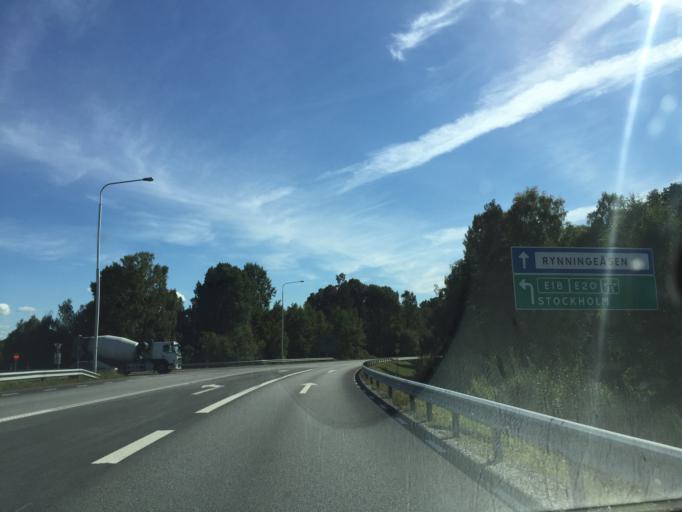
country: SE
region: OErebro
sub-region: Orebro Kommun
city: Orebro
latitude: 59.3037
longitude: 15.2586
